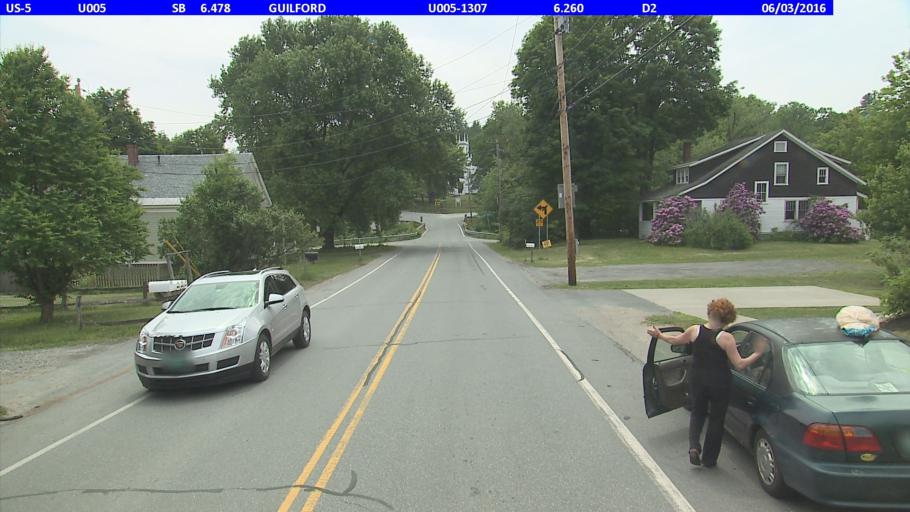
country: US
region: Vermont
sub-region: Windham County
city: Brattleboro
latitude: 42.8175
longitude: -72.5752
